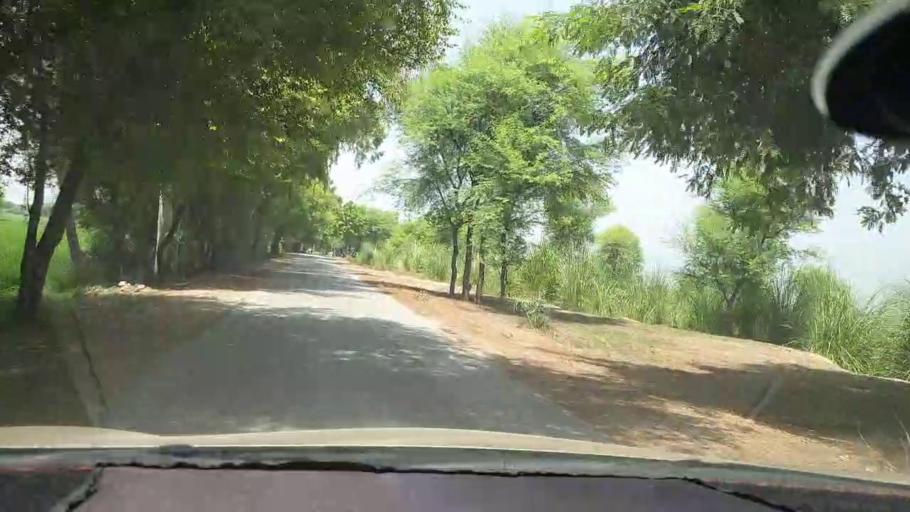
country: PK
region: Sindh
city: Kambar
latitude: 27.6605
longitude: 67.9488
